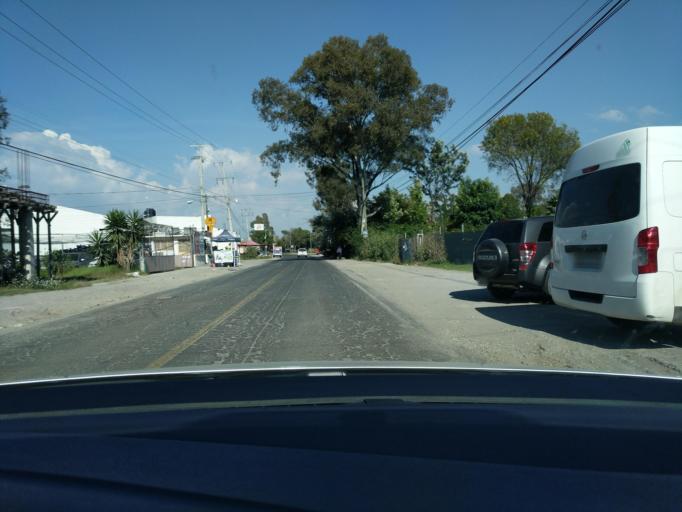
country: MX
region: Puebla
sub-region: San Gregorio Atzompa
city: Chipilo de Francisco Javier Mina
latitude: 19.0084
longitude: -98.3254
